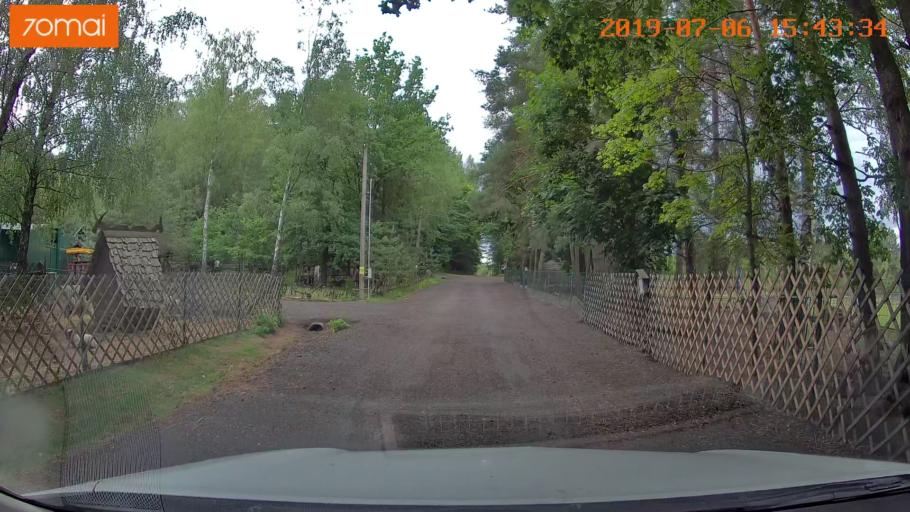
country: BY
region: Minsk
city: Rakaw
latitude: 53.9893
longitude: 26.9765
